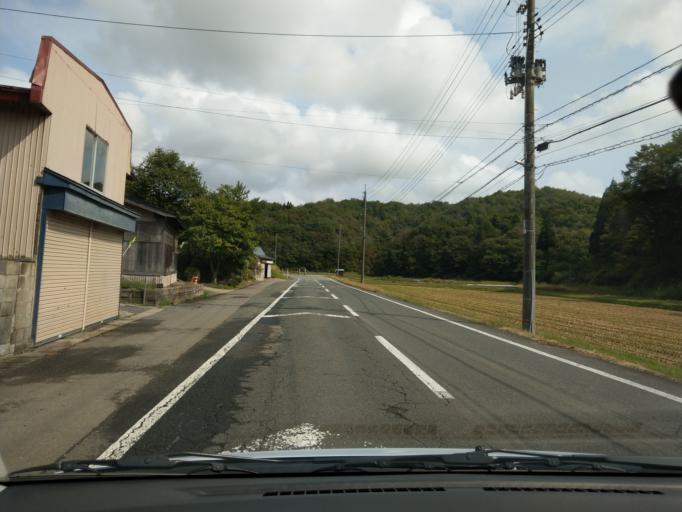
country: JP
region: Akita
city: Omagari
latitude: 39.5019
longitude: 140.3111
